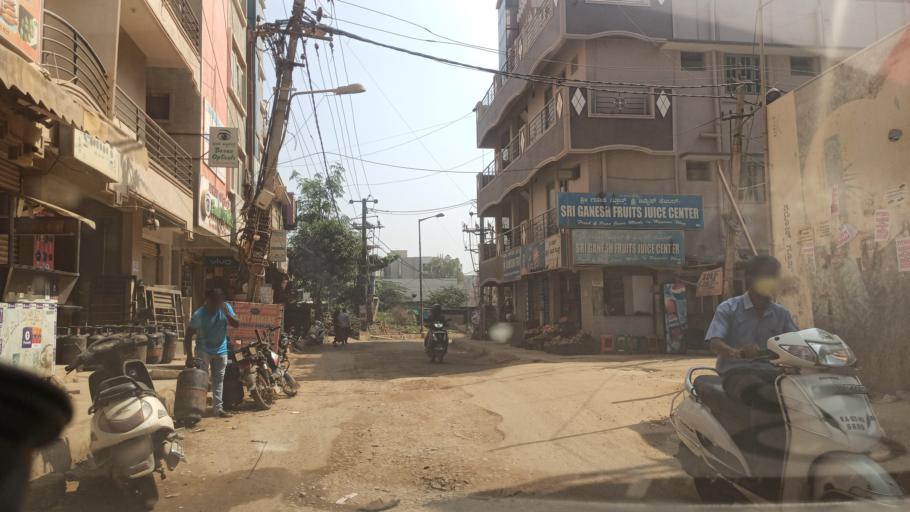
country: IN
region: Karnataka
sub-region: Bangalore Urban
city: Bangalore
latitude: 12.9497
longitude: 77.7014
